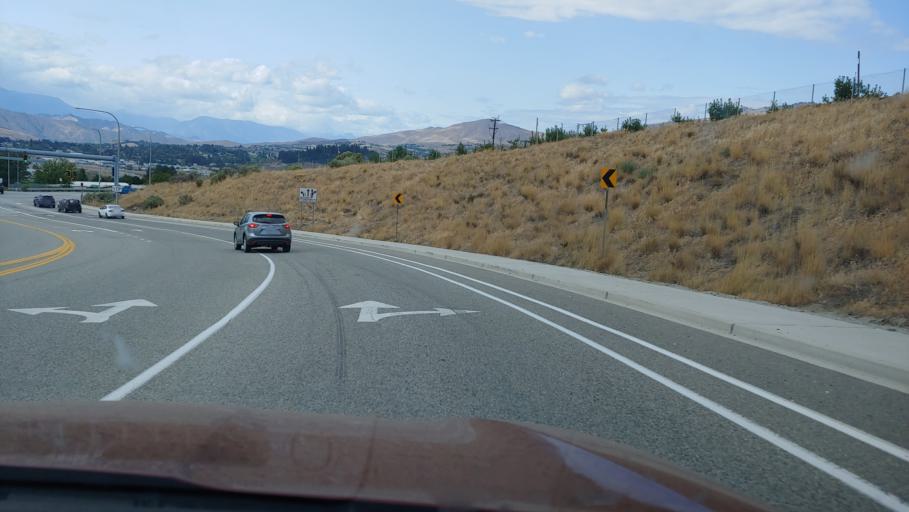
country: US
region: Washington
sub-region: Chelan County
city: Sunnyslope
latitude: 47.4679
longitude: -120.2976
